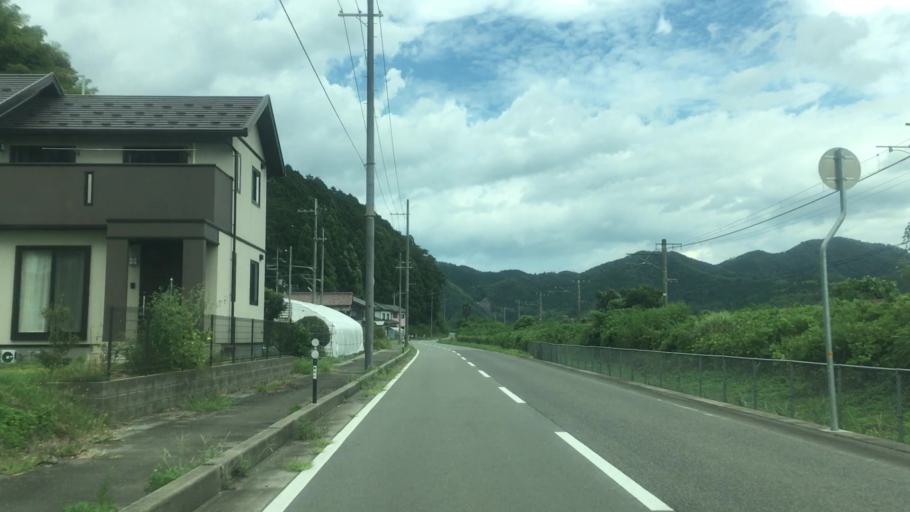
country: JP
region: Hyogo
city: Toyooka
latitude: 35.5697
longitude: 134.8042
